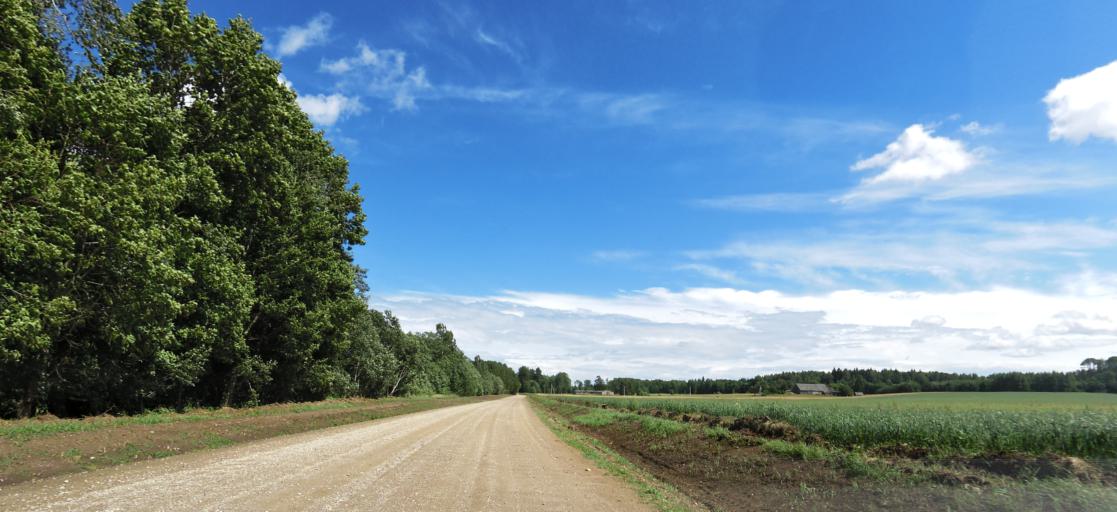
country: LT
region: Panevezys
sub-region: Birzai
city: Birzai
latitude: 56.4102
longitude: 24.8277
